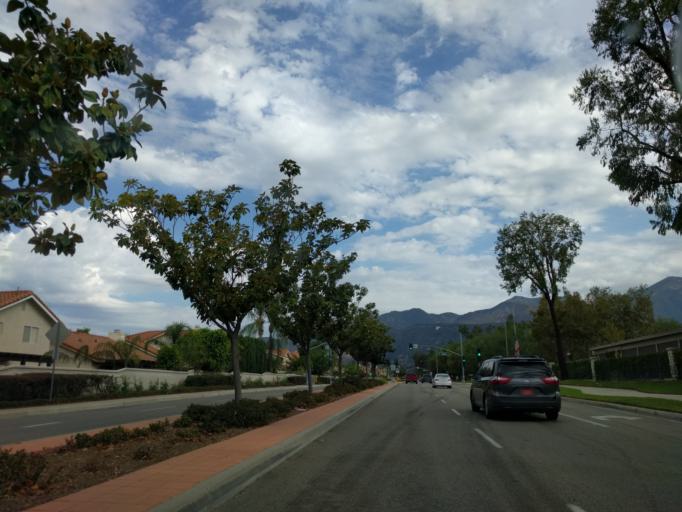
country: US
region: California
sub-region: Orange County
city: Trabuco Canyon
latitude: 33.6507
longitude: -117.5772
